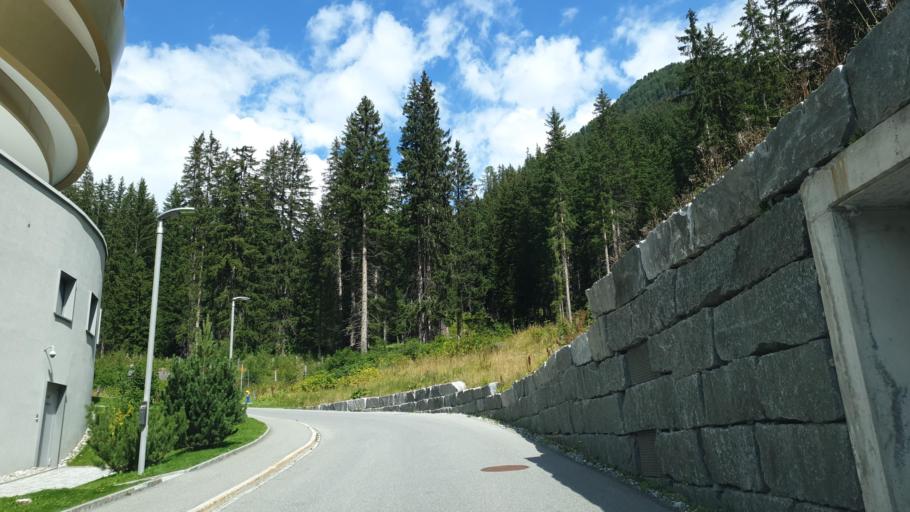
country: CH
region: Grisons
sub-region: Praettigau/Davos District
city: Davos
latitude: 46.8128
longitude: 9.8539
